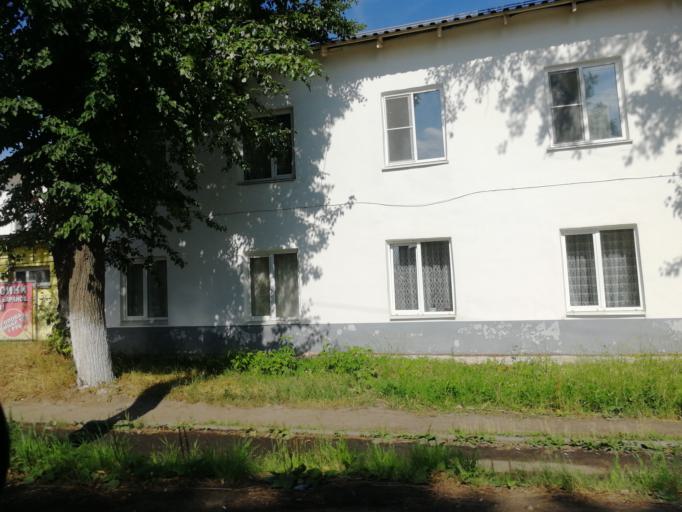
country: RU
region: Tula
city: Bogoroditsk
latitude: 53.7676
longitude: 38.1225
